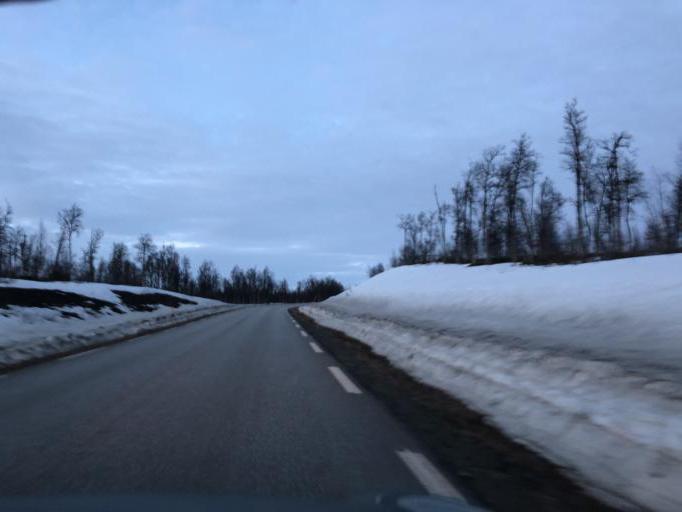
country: NO
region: Sor-Trondelag
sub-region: Tydal
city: Aas
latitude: 62.6987
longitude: 11.7876
